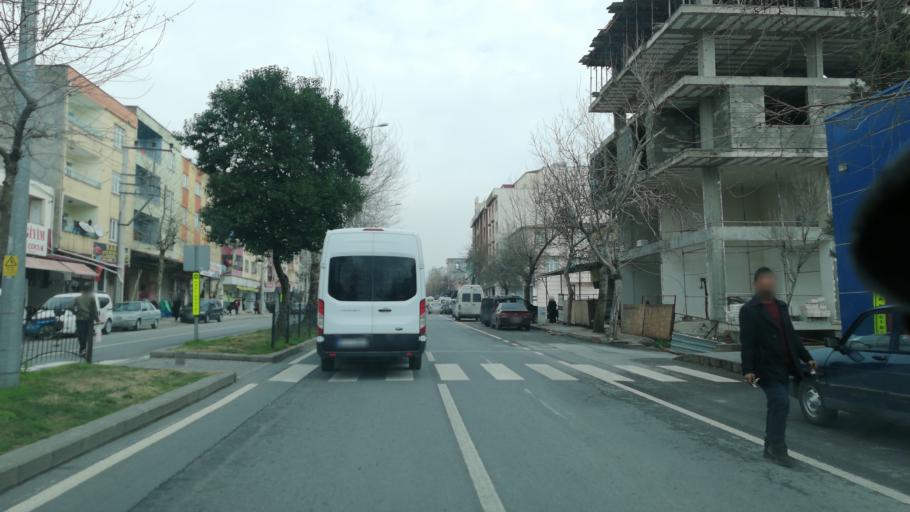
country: TR
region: Kahramanmaras
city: Kahramanmaras
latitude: 37.5720
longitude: 36.8956
